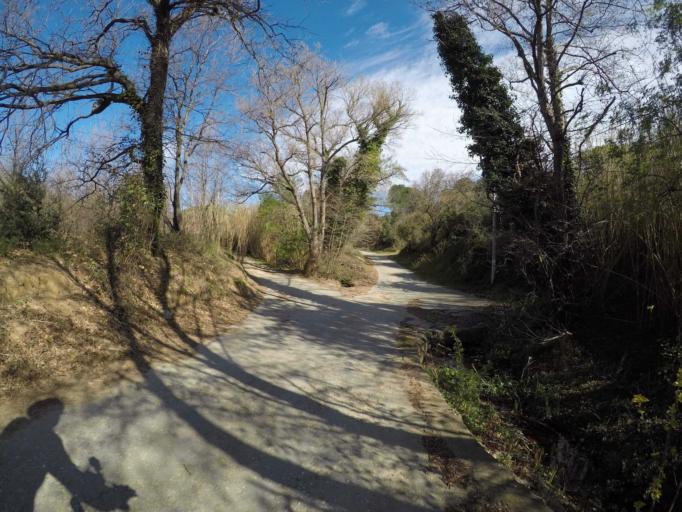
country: FR
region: Languedoc-Roussillon
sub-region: Departement des Pyrenees-Orientales
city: Millas
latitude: 42.7030
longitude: 2.7063
